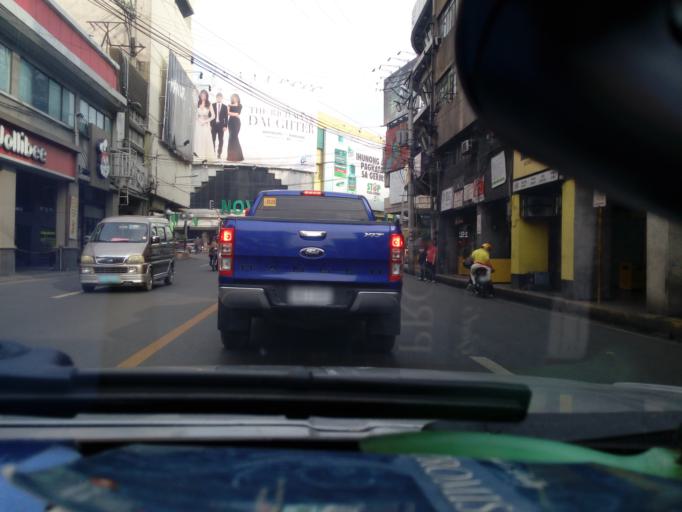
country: PH
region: Central Visayas
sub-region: Cebu City
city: Calero
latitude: 10.2960
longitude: 123.8988
